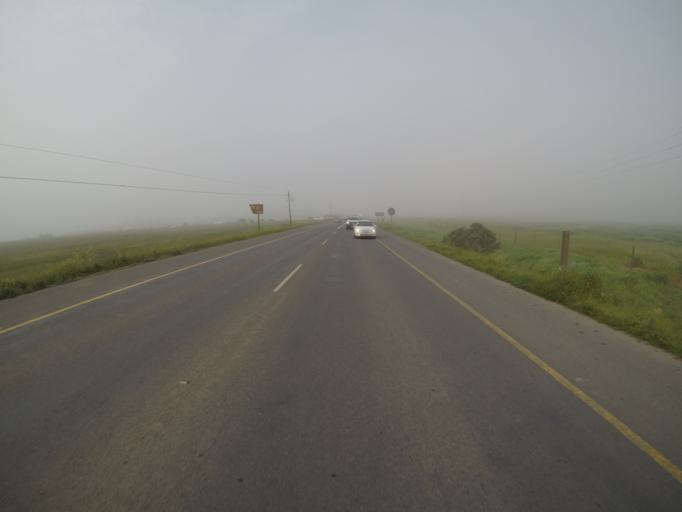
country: ZA
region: Western Cape
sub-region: City of Cape Town
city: Kraaifontein
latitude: -33.7833
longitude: 18.7042
